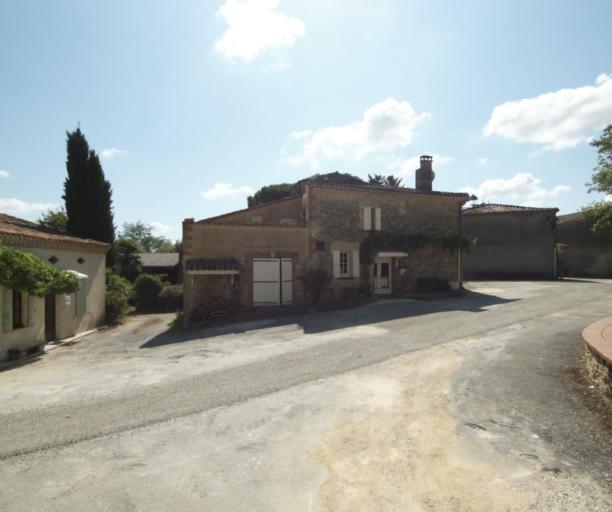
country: FR
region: Midi-Pyrenees
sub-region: Departement de la Haute-Garonne
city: Auriac-sur-Vendinelle
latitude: 43.4495
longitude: 1.7892
